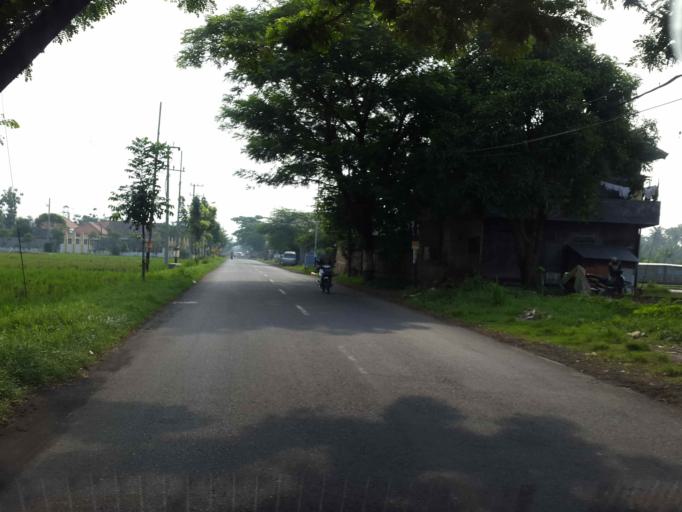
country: ID
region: East Java
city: Kambingan
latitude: -7.9674
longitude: 112.6824
